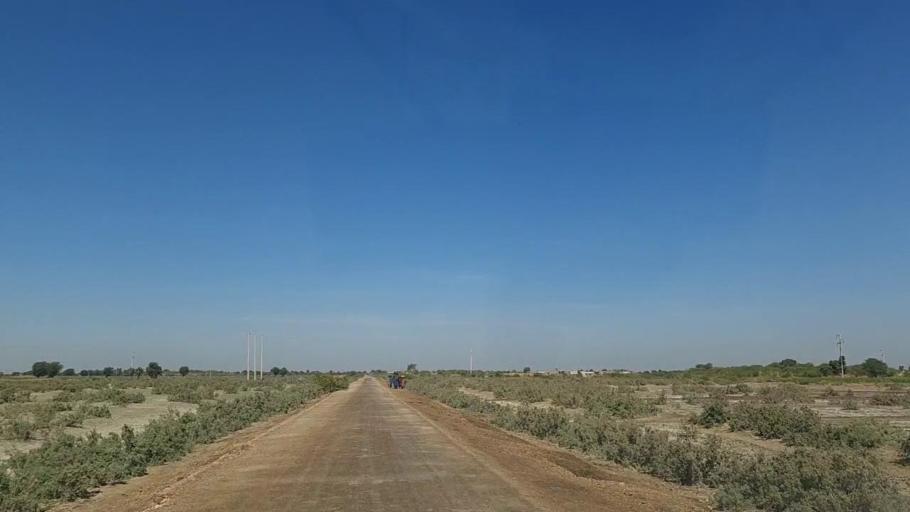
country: PK
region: Sindh
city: Samaro
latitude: 25.3006
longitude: 69.4858
